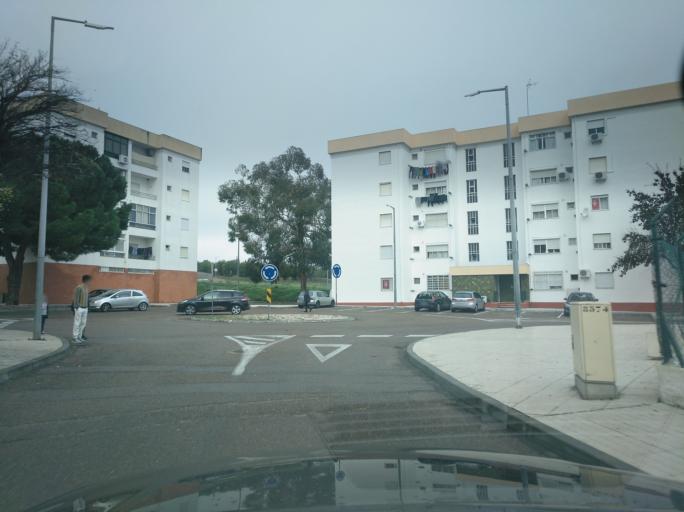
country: PT
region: Portalegre
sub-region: Elvas
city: Elvas
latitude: 38.8685
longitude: -7.1709
